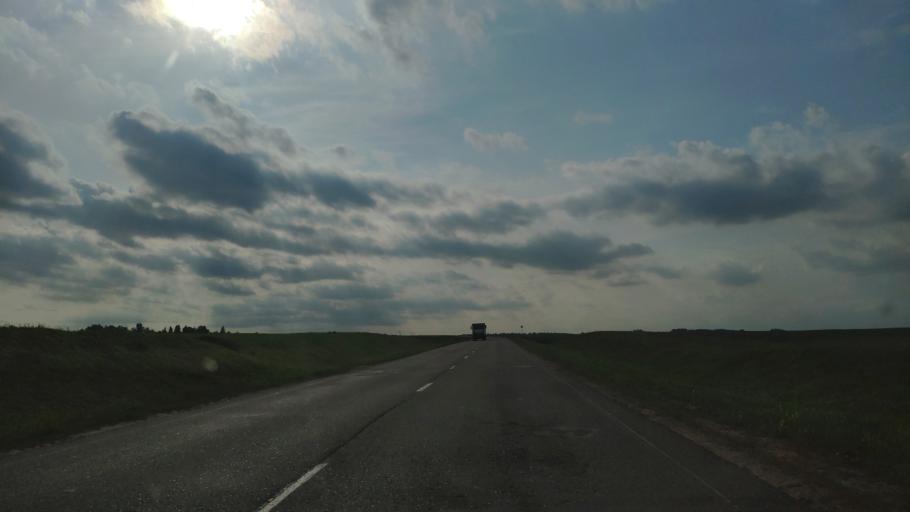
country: BY
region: Minsk
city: Azyartso
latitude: 53.8358
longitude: 27.3432
